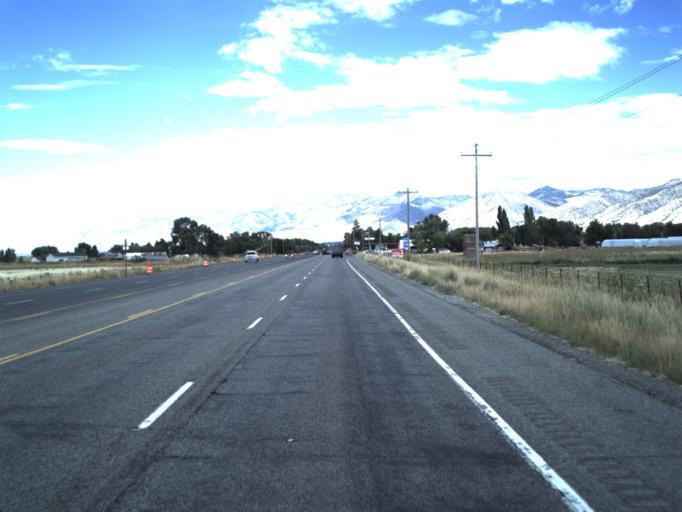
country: US
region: Utah
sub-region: Cache County
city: Hyrum
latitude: 41.6726
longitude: -111.8858
